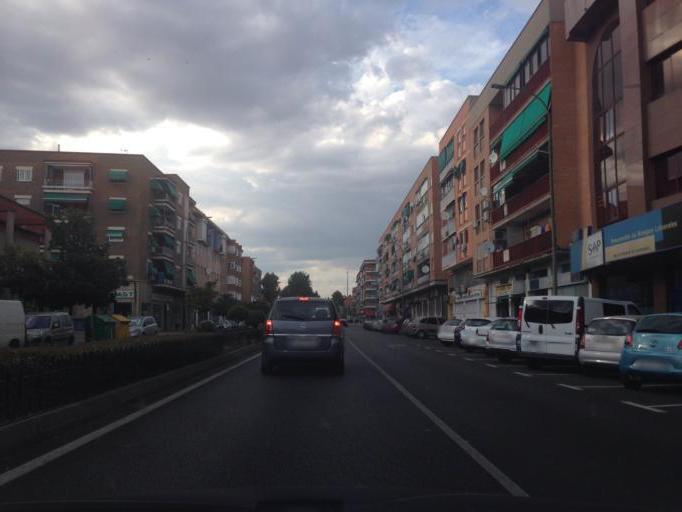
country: ES
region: Madrid
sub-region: Provincia de Madrid
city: Torrejon de Ardoz
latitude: 40.4596
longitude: -3.4836
